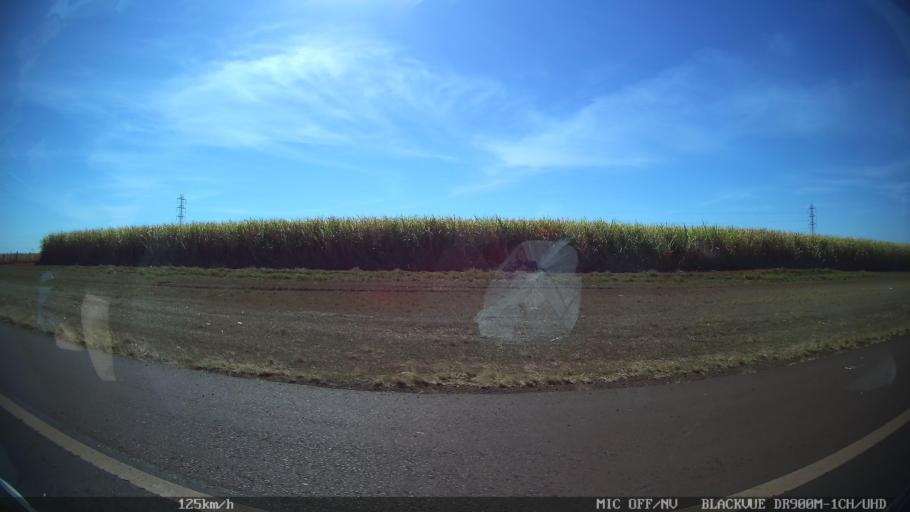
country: BR
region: Sao Paulo
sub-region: Guaira
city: Guaira
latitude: -20.4490
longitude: -48.1906
